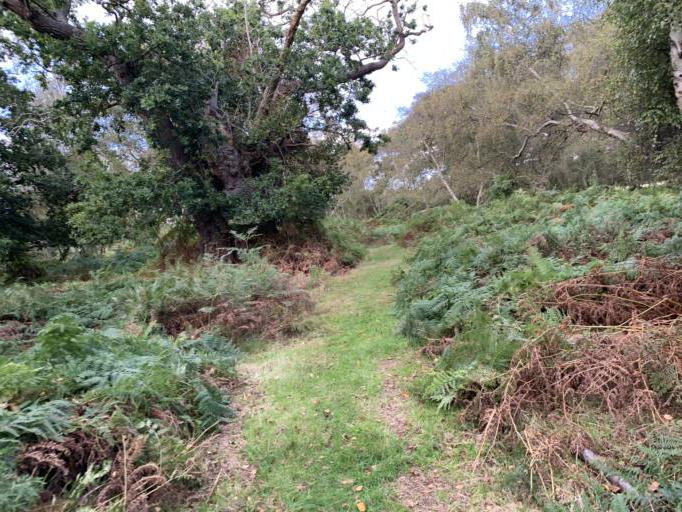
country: GB
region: England
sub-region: Suffolk
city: Aldeburgh
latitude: 52.1310
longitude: 1.5381
